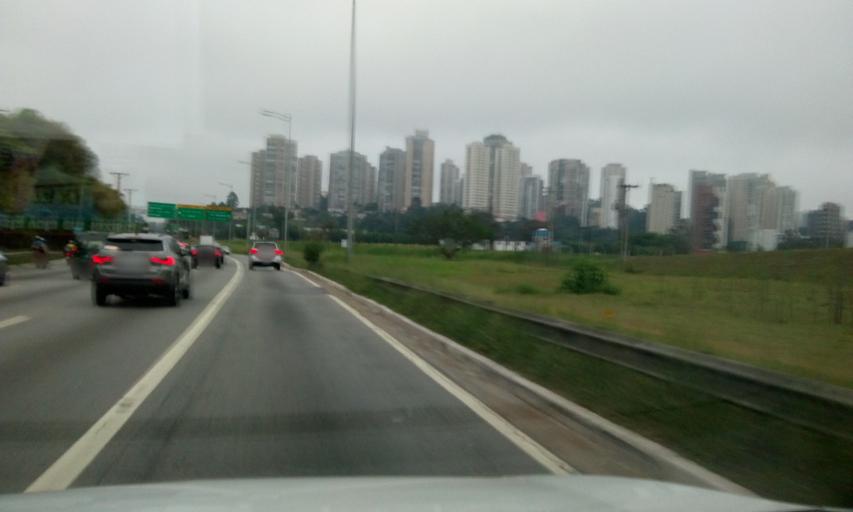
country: BR
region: Sao Paulo
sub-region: Taboao Da Serra
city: Taboao da Serra
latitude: -23.6250
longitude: -46.7117
